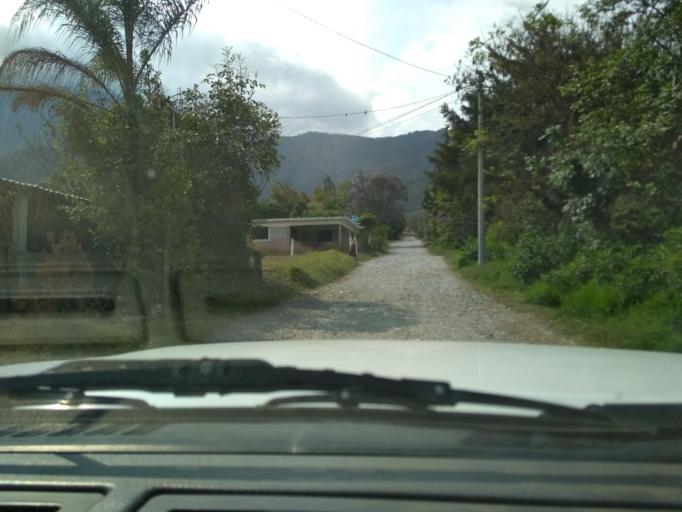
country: MX
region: Veracruz
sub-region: Acultzingo
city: Acatla
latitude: 18.7674
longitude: -97.2282
